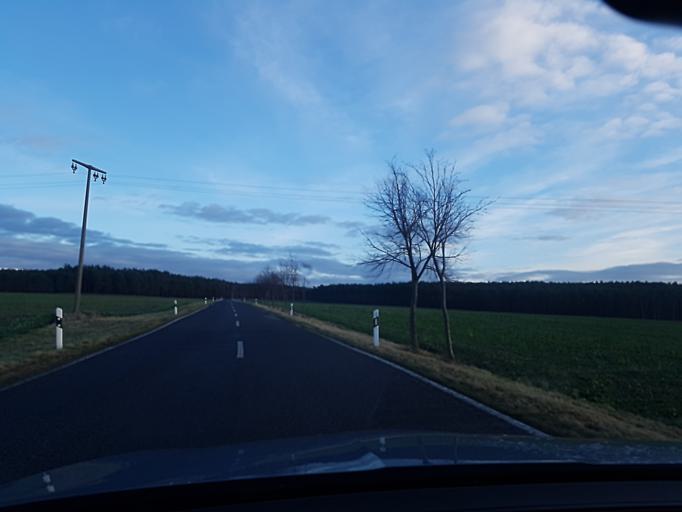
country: DE
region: Brandenburg
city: Trobitz
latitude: 51.5713
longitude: 13.4130
